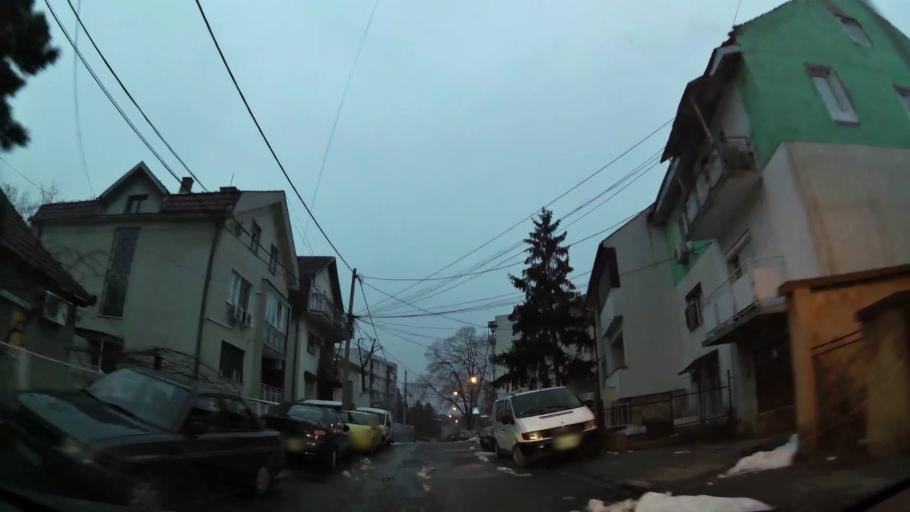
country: RS
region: Central Serbia
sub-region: Belgrade
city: Vozdovac
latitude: 44.7767
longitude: 20.4856
